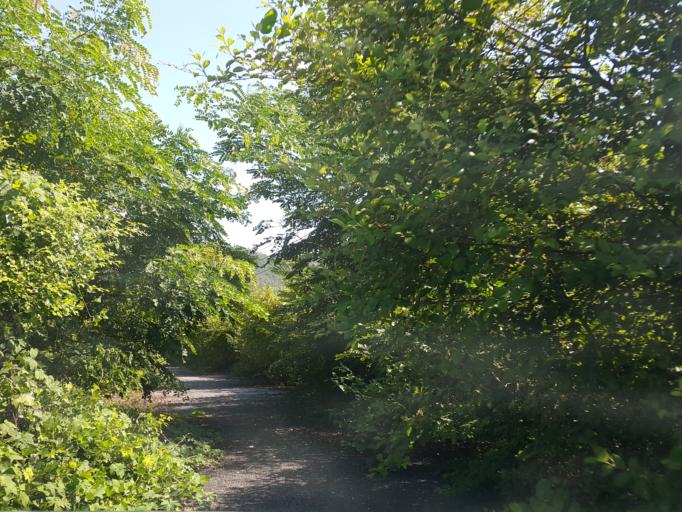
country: TH
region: Chiang Mai
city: Mae On
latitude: 18.8027
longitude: 99.1904
